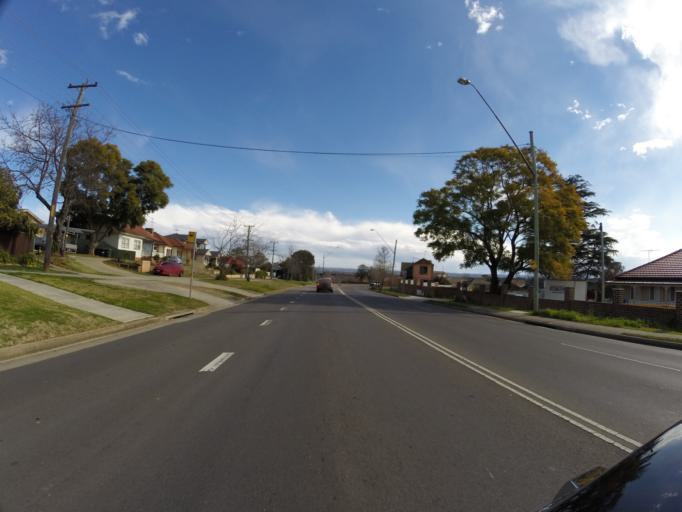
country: AU
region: New South Wales
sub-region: Camden
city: Narellan
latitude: -34.0430
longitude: 150.7279
